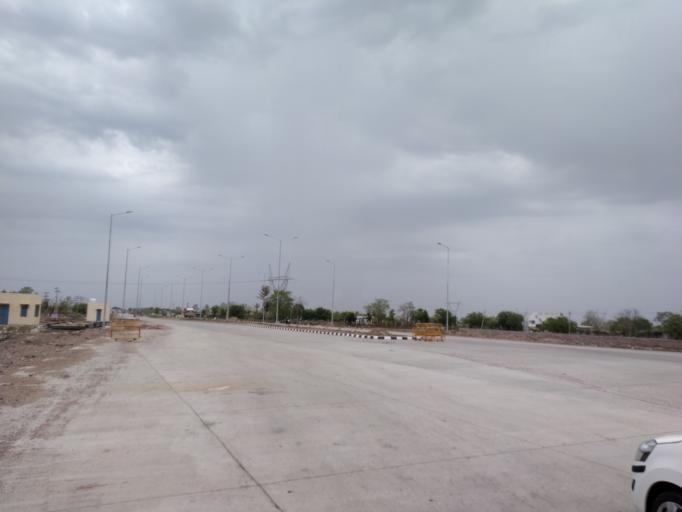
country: IN
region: Rajasthan
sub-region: Kota
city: Chechat
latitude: 24.9668
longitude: 75.9343
